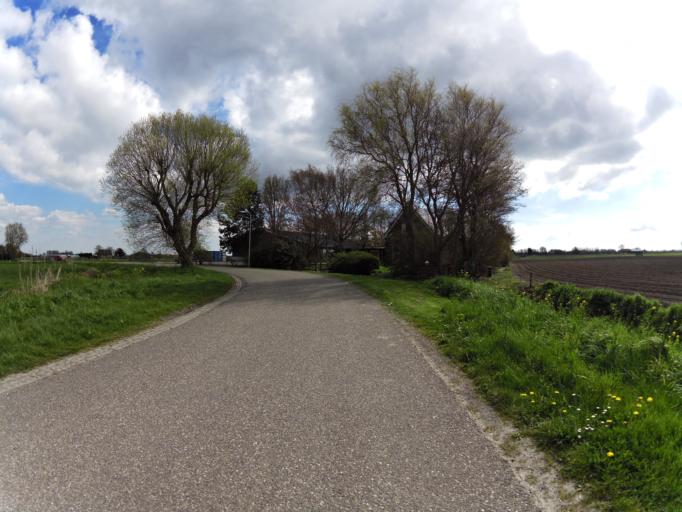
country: NL
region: South Holland
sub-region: Gemeente Hellevoetsluis
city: Nieuwenhoorn
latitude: 51.8872
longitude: 4.1191
